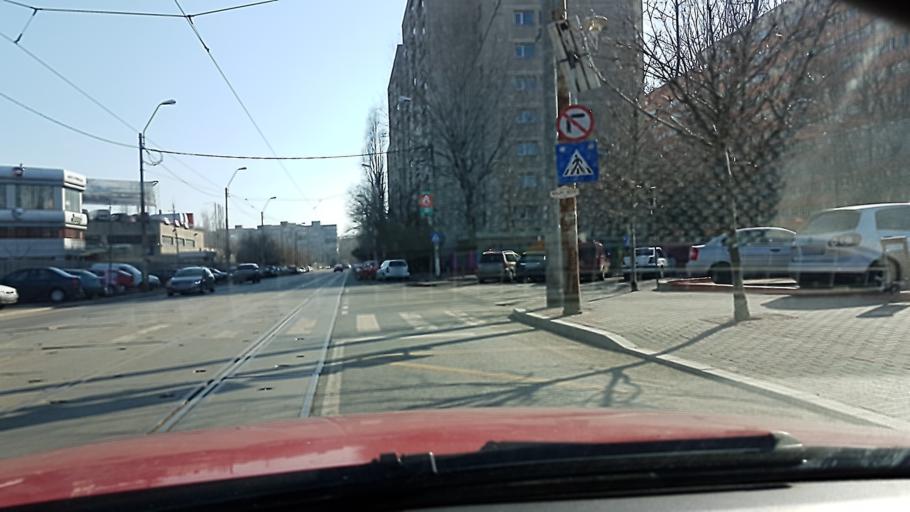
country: RO
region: Ilfov
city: Dobroesti
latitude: 44.4330
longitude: 26.1723
